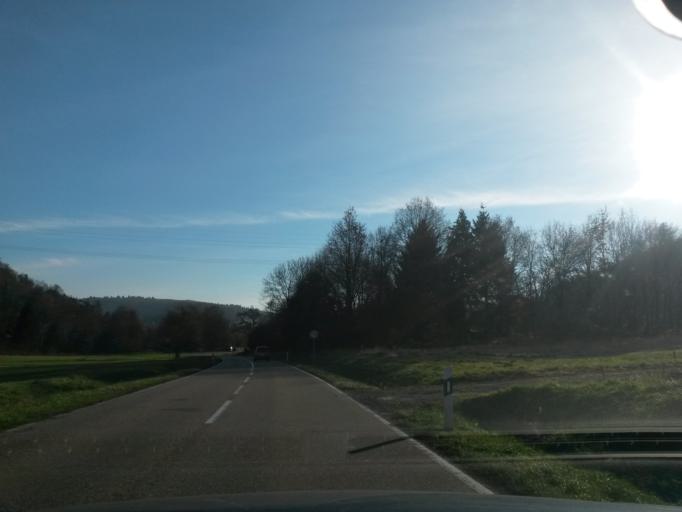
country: DE
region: Baden-Wuerttemberg
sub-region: Karlsruhe Region
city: Konigsbach-Stein
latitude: 48.9394
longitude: 8.6275
